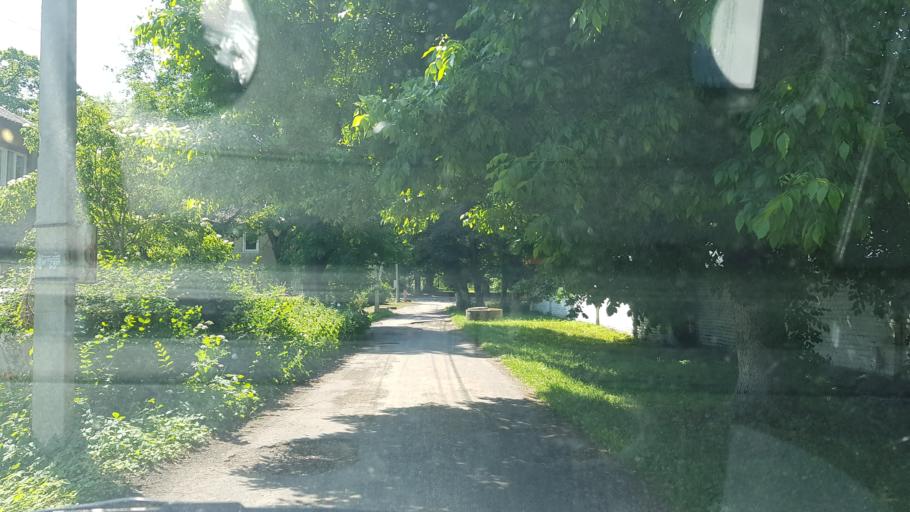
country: RU
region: Kaliningrad
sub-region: Gorod Kaliningrad
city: Baltiysk
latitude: 54.6467
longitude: 19.8878
